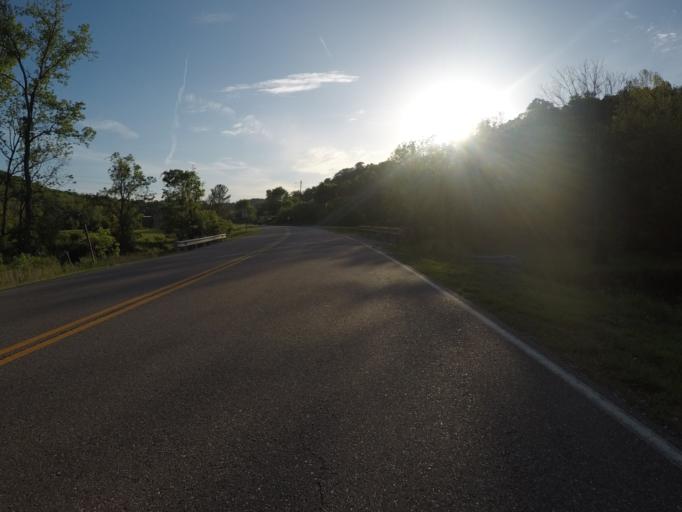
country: US
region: West Virginia
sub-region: Cabell County
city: Huntington
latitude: 38.5560
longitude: -82.4538
